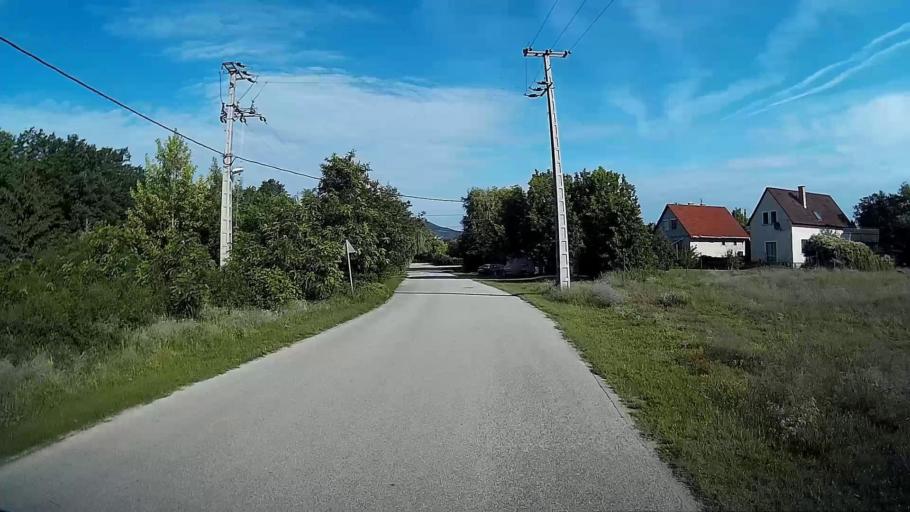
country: HU
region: Pest
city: God
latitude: 47.6829
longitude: 19.1085
